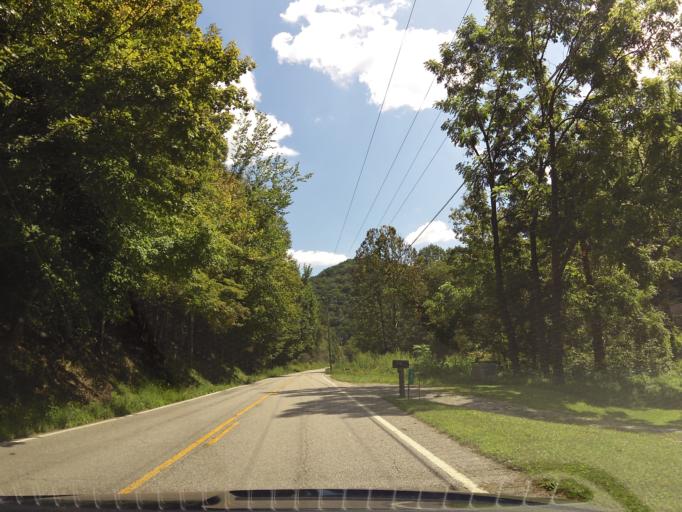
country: US
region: Kentucky
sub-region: Harlan County
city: Loyall
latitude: 36.9375
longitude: -83.3805
